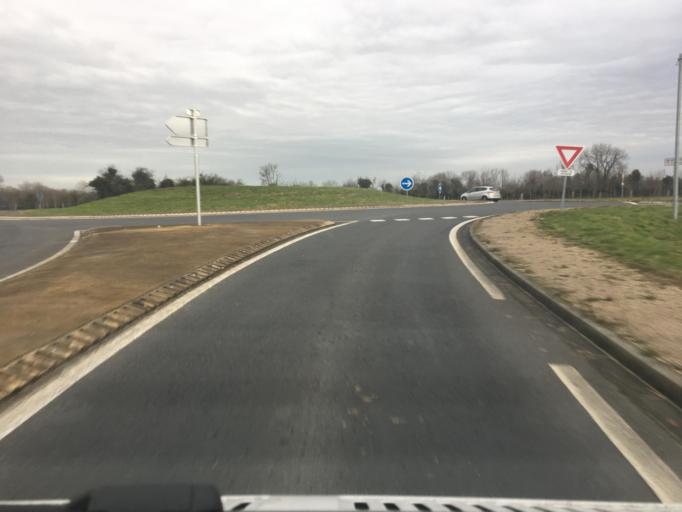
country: FR
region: Haute-Normandie
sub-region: Departement de l'Eure
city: Beuzeville
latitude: 49.3311
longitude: 0.3136
